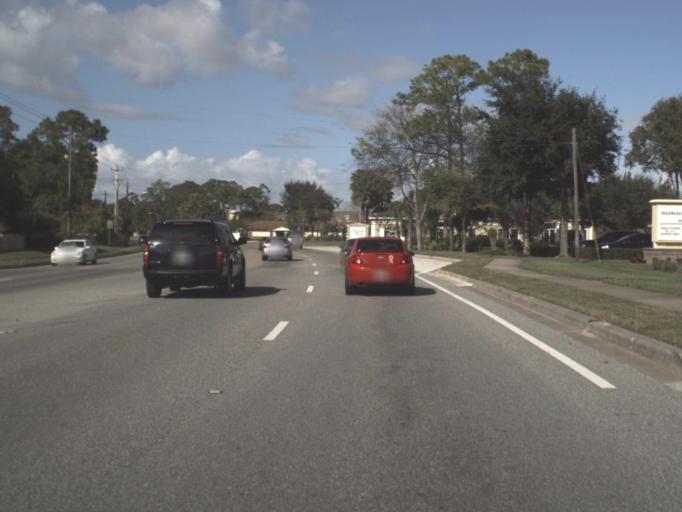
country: US
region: Florida
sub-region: Volusia County
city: South Daytona
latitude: 29.1512
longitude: -81.0351
